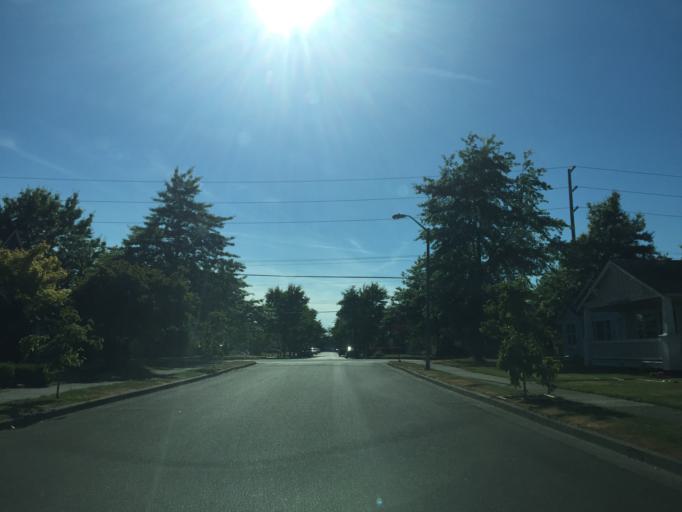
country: US
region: Washington
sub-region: Whatcom County
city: Lynden
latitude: 48.9615
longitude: -122.4291
